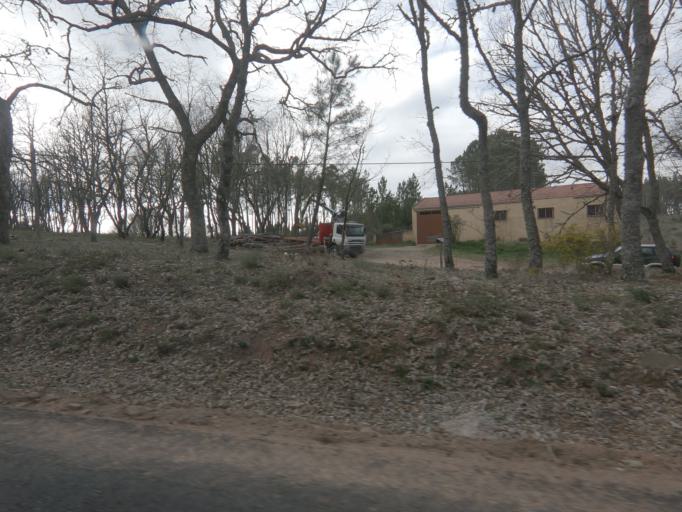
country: ES
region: Castille and Leon
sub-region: Provincia de Salamanca
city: Villasrubias
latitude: 40.3339
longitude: -6.6440
